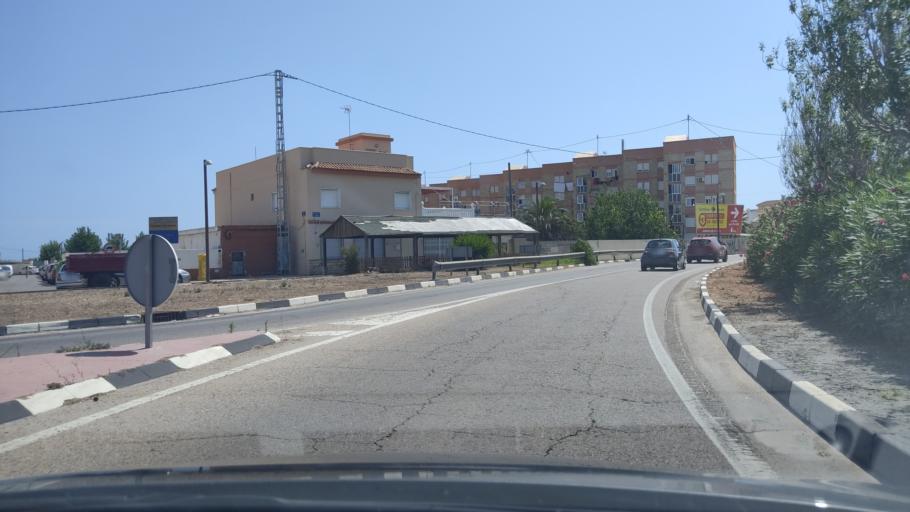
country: ES
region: Valencia
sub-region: Provincia de Valencia
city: Sollana
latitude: 39.3071
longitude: -0.2974
